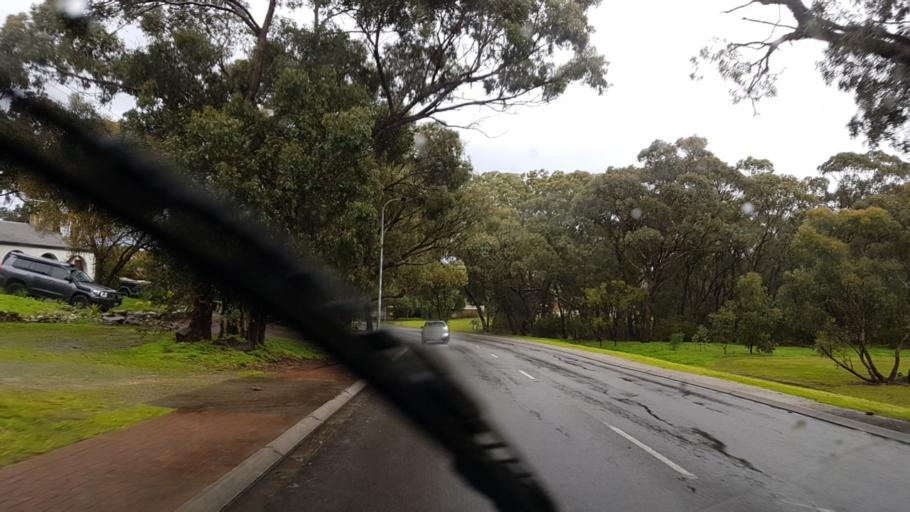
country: AU
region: South Australia
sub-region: Onkaparinga
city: Craigburn Farm
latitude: -35.0591
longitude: 138.5986
